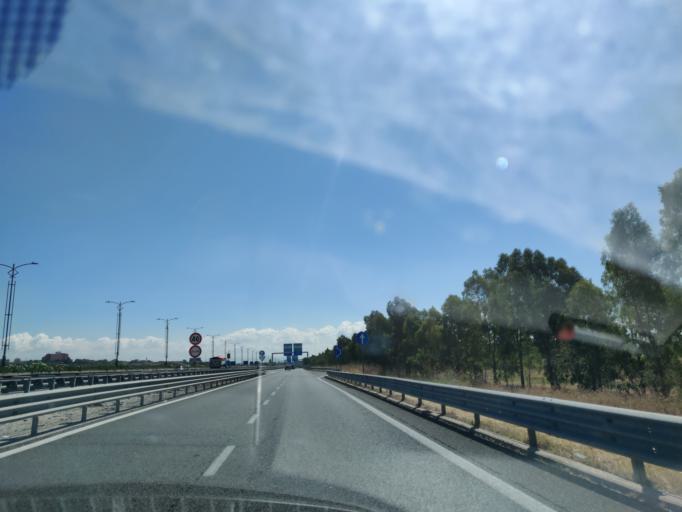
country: IT
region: Latium
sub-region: Citta metropolitana di Roma Capitale
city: Vitinia
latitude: 41.8165
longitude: 12.3725
